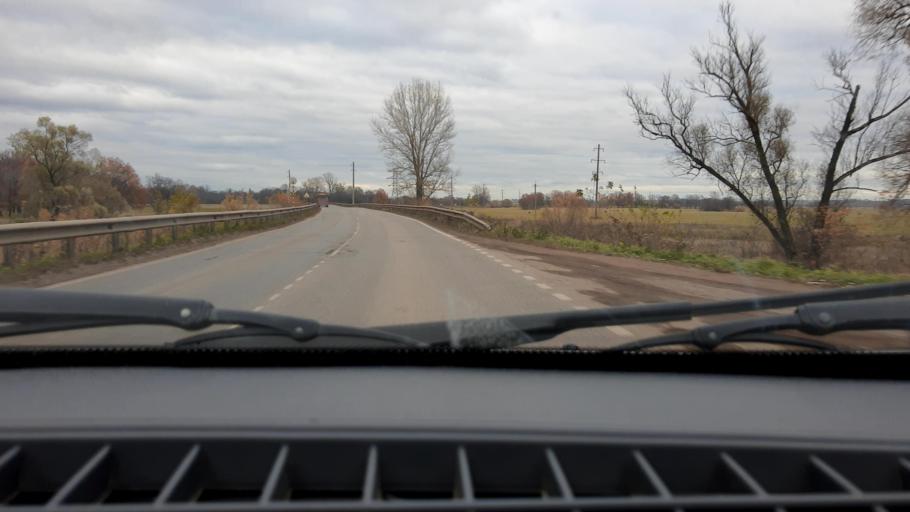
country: RU
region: Bashkortostan
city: Kabakovo
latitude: 54.5678
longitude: 55.9804
